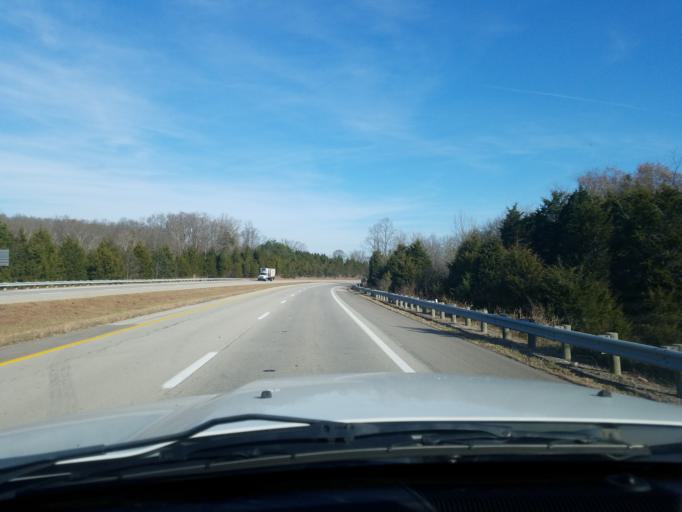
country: US
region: Ohio
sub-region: Adams County
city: Peebles
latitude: 38.9472
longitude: -83.3797
